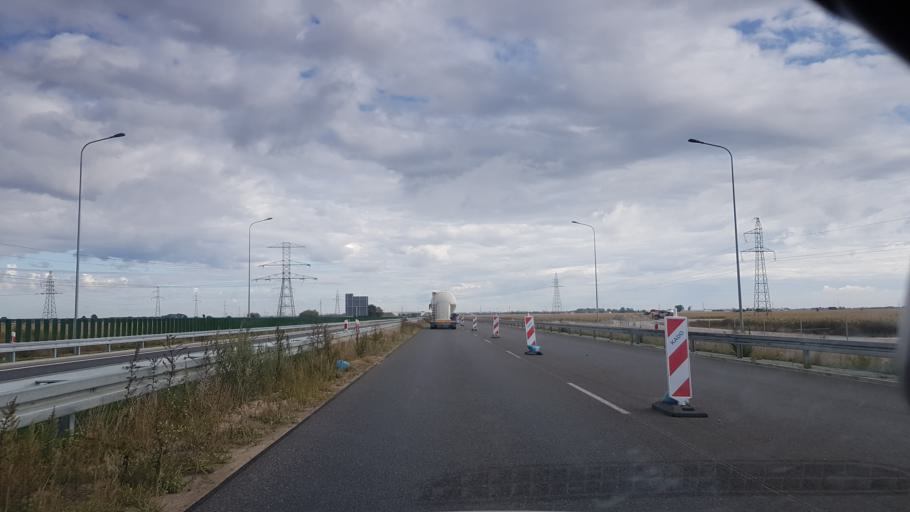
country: PL
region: Greater Poland Voivodeship
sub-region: Powiat poznanski
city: Steszew
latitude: 52.3362
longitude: 16.7381
